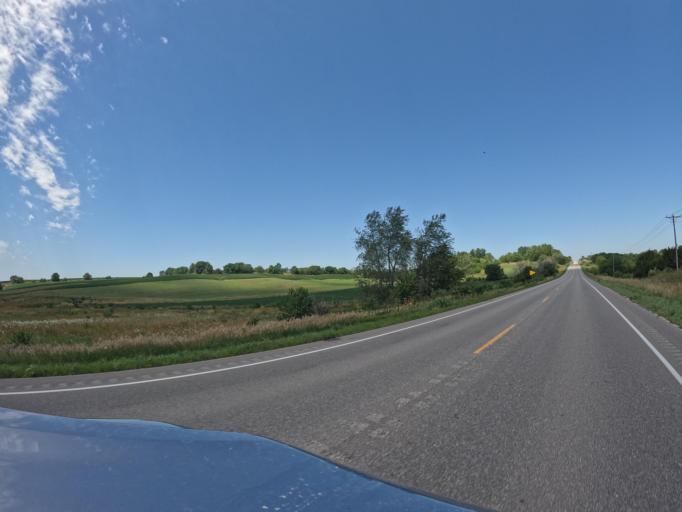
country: US
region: Iowa
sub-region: Keokuk County
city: Sigourney
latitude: 41.4423
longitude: -92.3550
